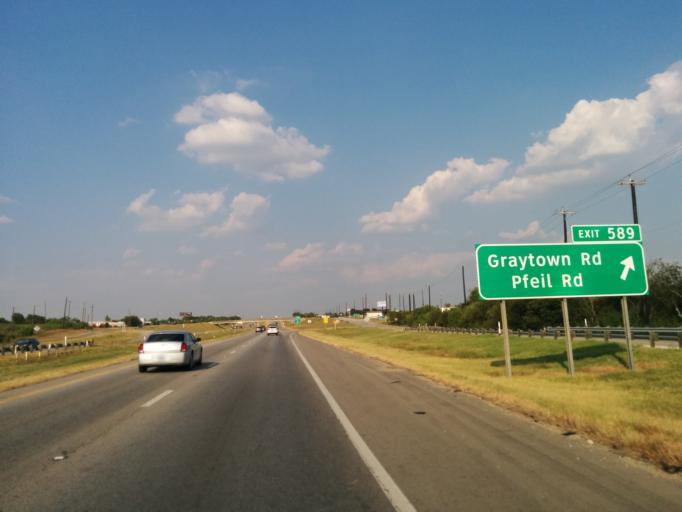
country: US
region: Texas
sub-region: Bexar County
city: Converse
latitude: 29.4726
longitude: -98.2693
